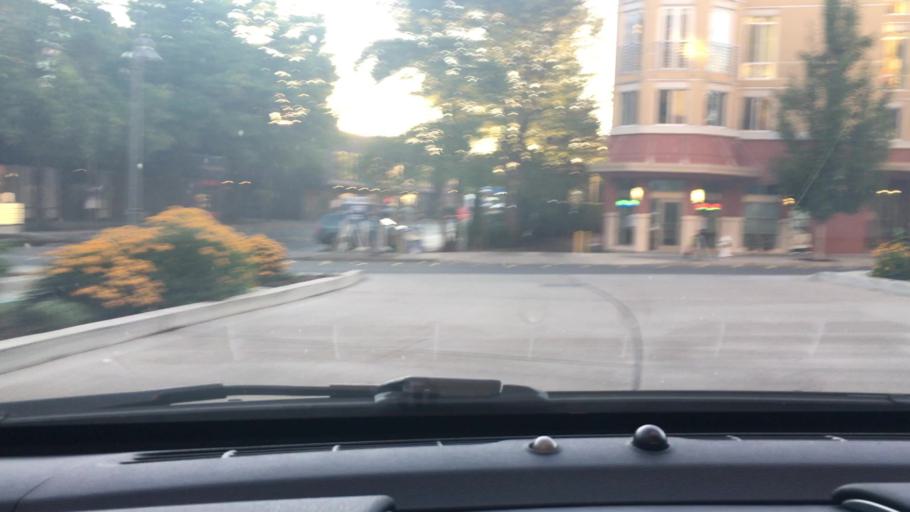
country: US
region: Washington
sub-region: King County
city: Mercer Island
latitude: 47.5875
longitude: -122.2378
